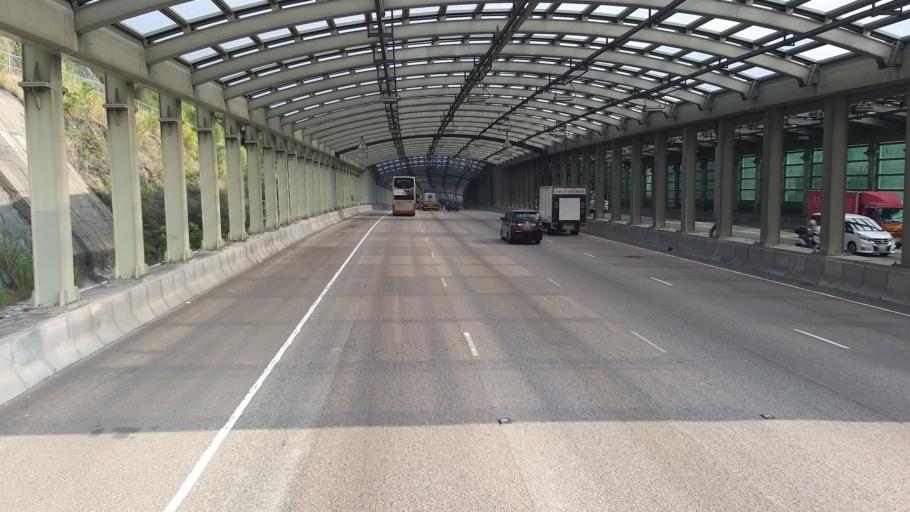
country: HK
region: Tuen Mun
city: Tuen Mun
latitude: 22.3811
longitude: 113.9830
